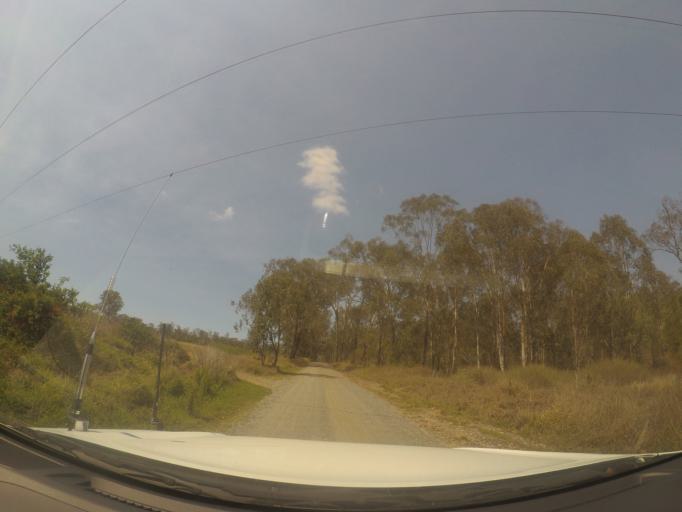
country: AU
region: Queensland
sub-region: Logan
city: North Maclean
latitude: -27.7739
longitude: 153.0383
